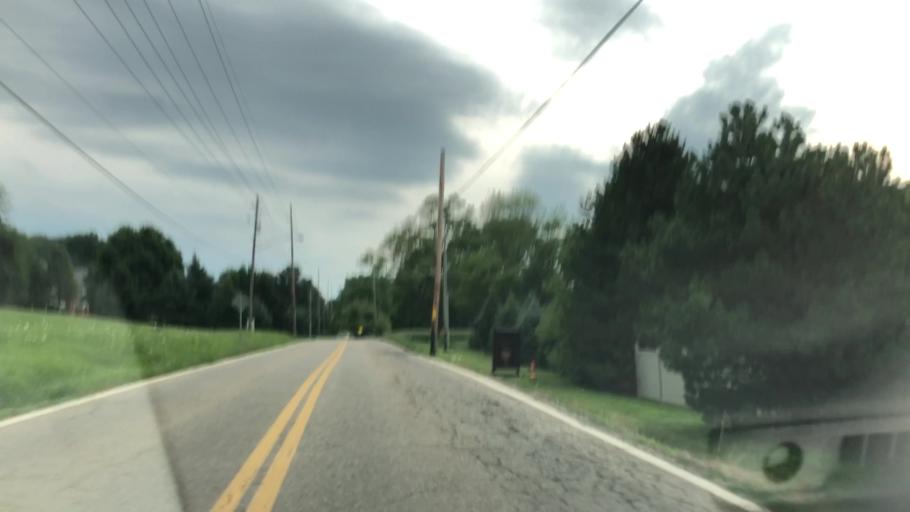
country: US
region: Ohio
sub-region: Stark County
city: Perry Heights
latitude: 40.8105
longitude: -81.4900
